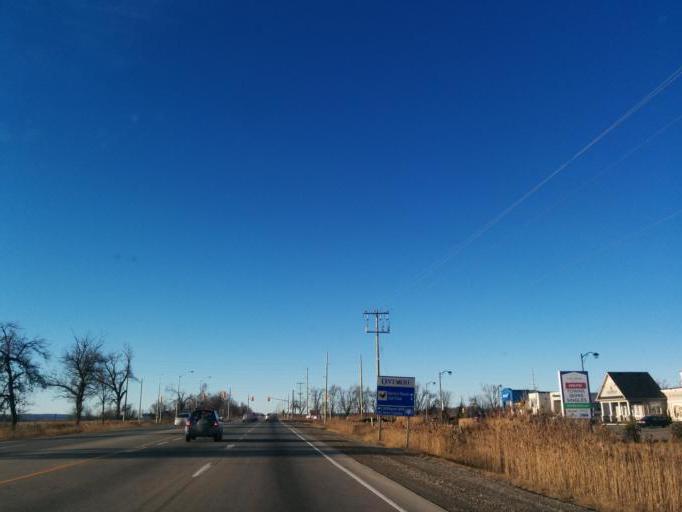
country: CA
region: Ontario
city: Brampton
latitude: 43.7526
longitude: -79.8501
